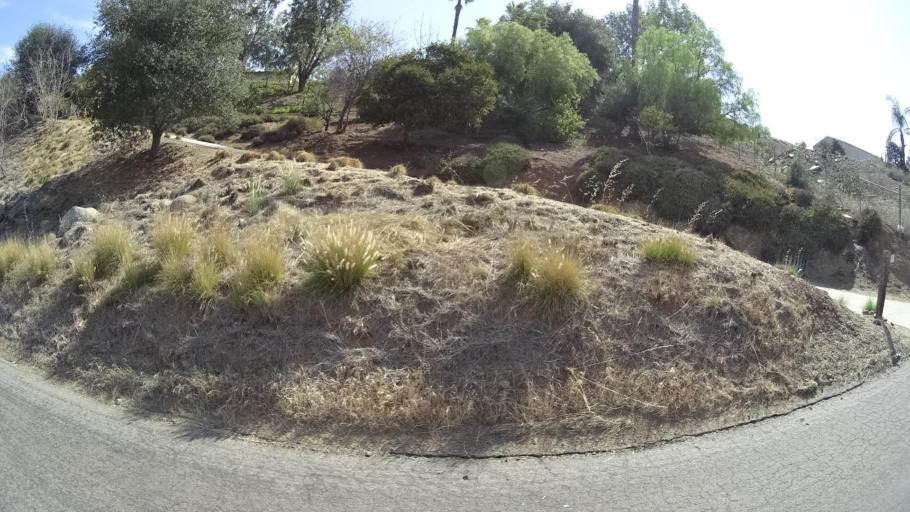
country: US
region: California
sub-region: San Diego County
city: Hidden Meadows
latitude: 33.2174
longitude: -117.1726
